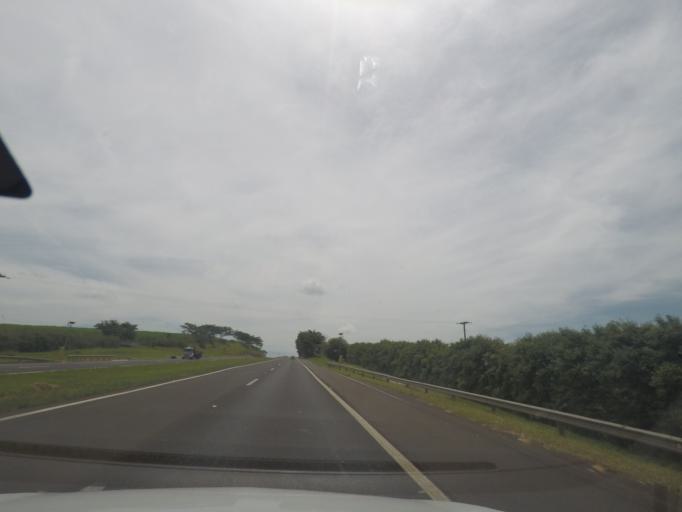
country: BR
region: Sao Paulo
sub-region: Bebedouro
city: Bebedouro
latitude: -21.0266
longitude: -48.4220
